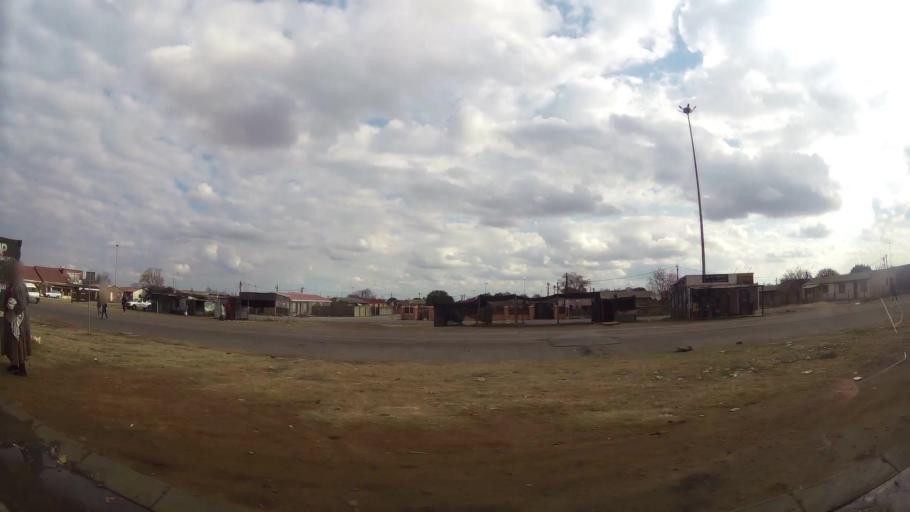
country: ZA
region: Orange Free State
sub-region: Fezile Dabi District Municipality
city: Sasolburg
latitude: -26.8396
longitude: 27.8453
